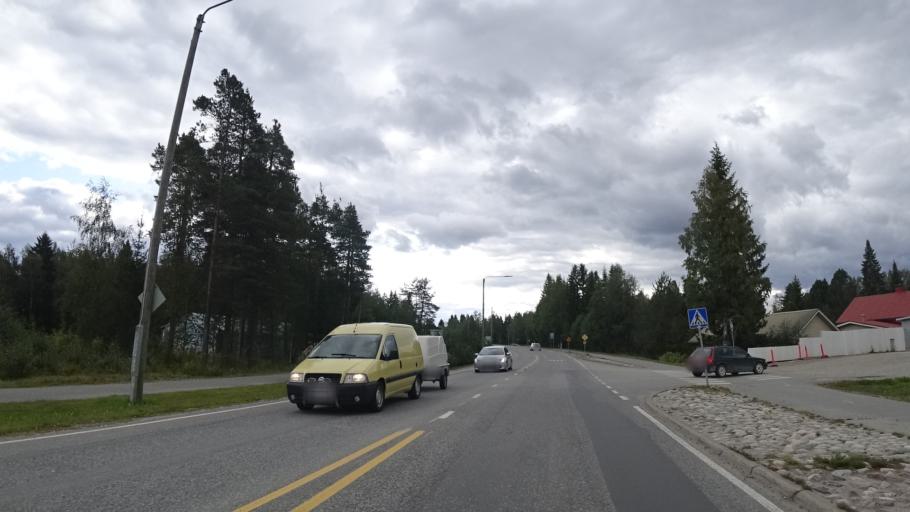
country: FI
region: North Karelia
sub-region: Joensuu
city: Ilomantsi
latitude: 62.6676
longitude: 30.9385
